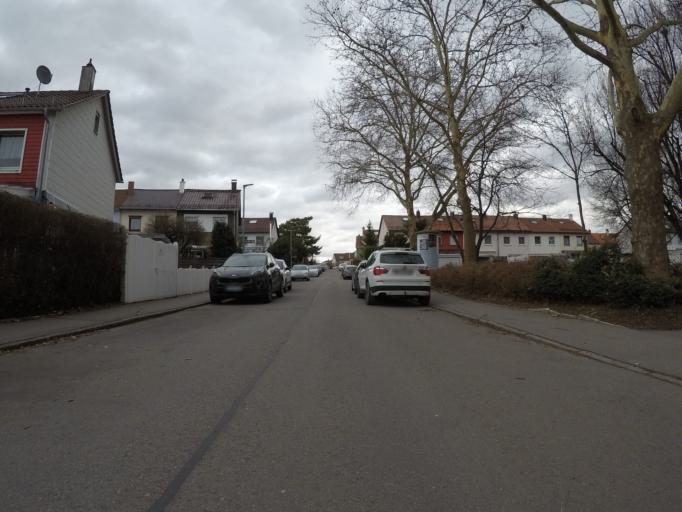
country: DE
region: Baden-Wuerttemberg
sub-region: Tuebingen Region
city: Reutlingen
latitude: 48.5083
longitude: 9.2132
